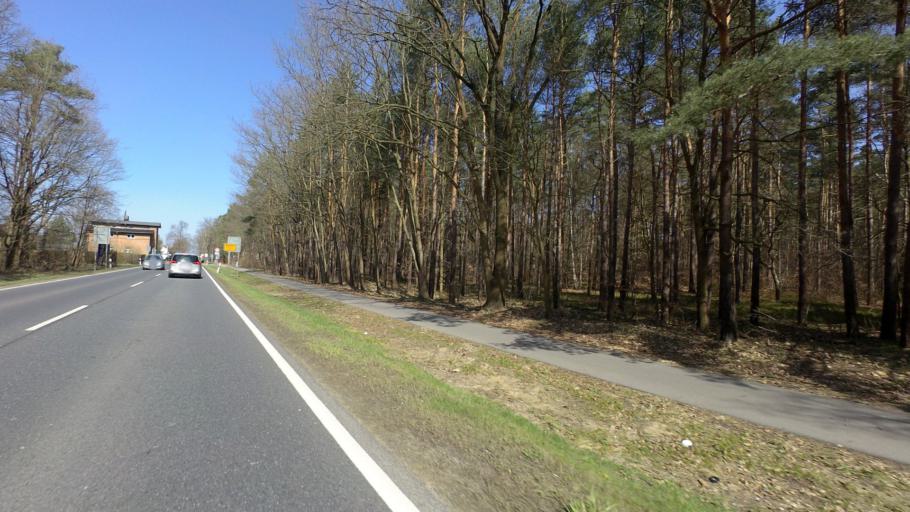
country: DE
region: Brandenburg
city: Oranienburg
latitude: 52.8066
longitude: 13.2268
